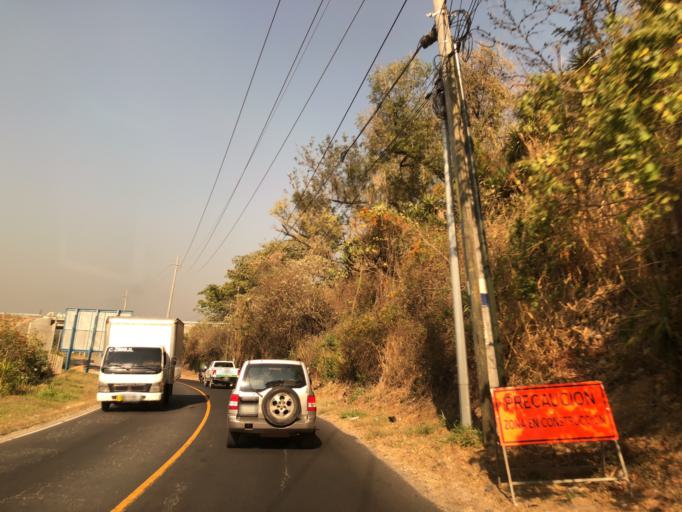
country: GT
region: Guatemala
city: Petapa
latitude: 14.5021
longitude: -90.5414
